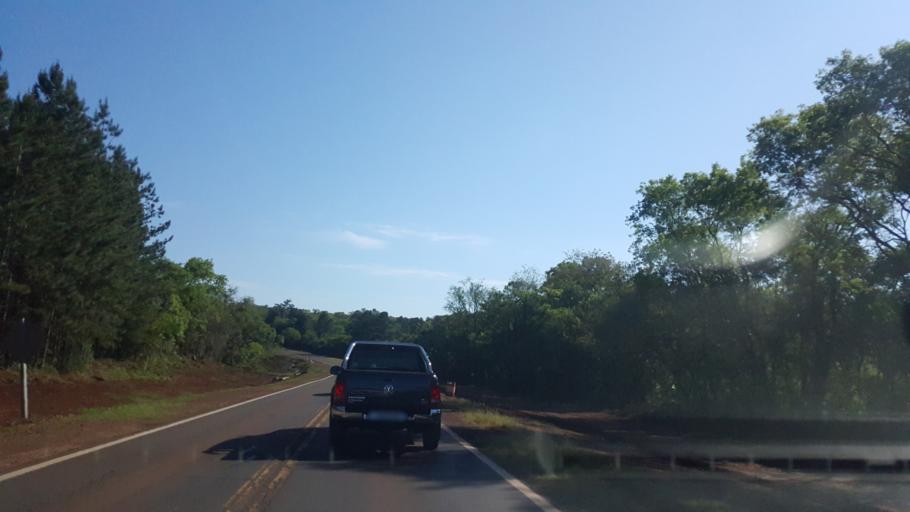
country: AR
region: Misiones
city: Santa Ana
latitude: -27.3653
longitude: -55.5586
